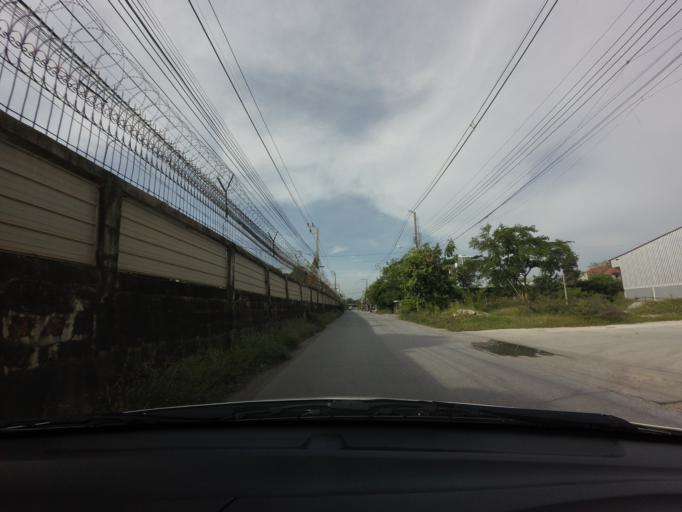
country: TH
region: Bangkok
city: Bang Na
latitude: 13.6525
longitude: 100.6564
